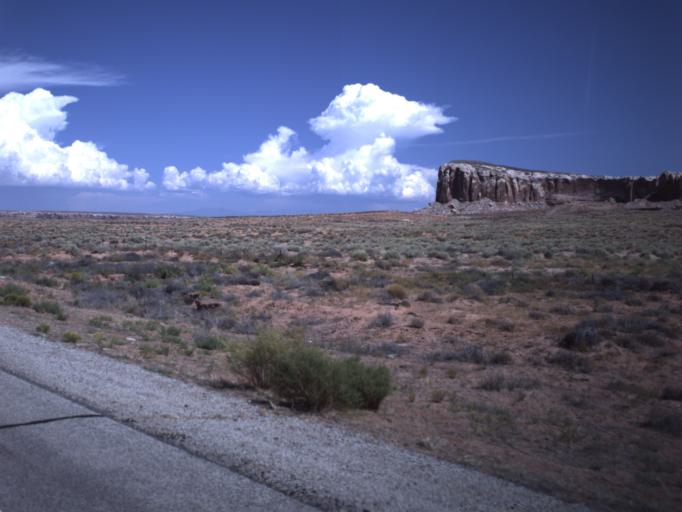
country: US
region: Utah
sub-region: San Juan County
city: Blanding
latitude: 37.2205
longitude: -109.6159
